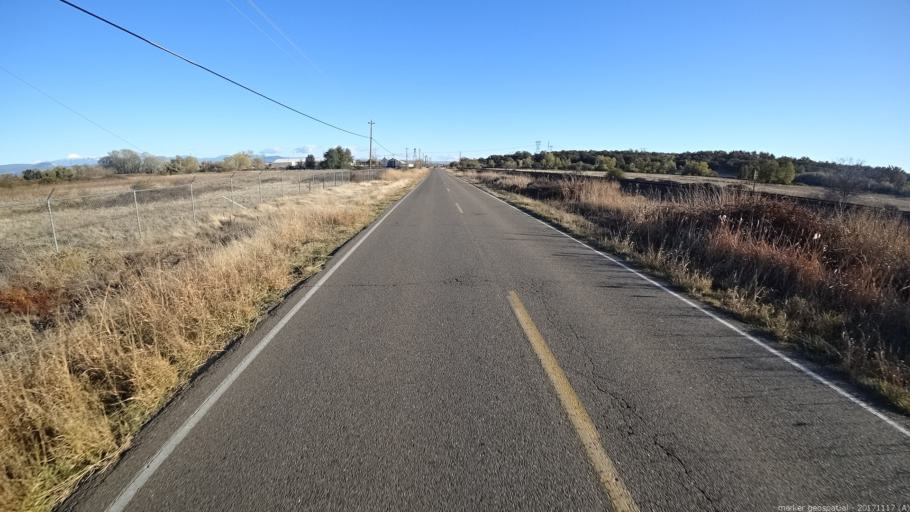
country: US
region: California
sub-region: Shasta County
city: Cottonwood
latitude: 40.4216
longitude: -122.2583
